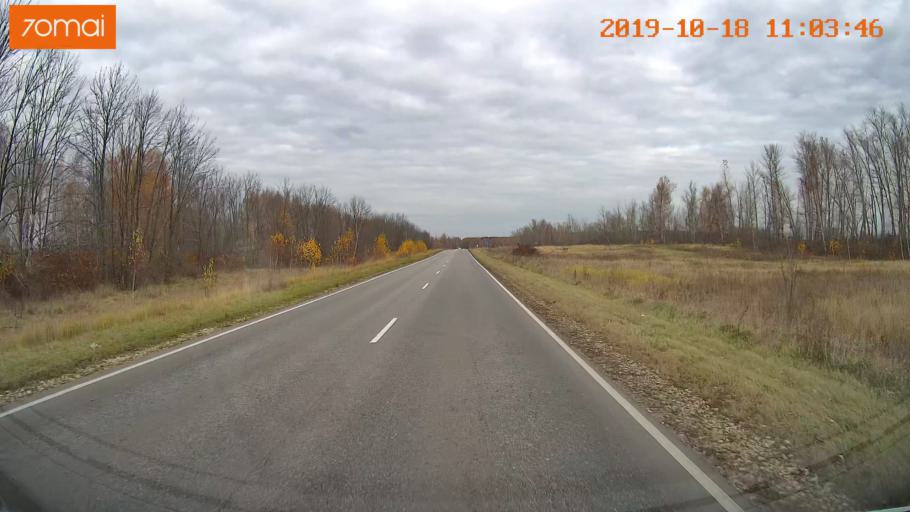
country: RU
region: Tula
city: Yepifan'
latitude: 53.8847
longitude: 38.5494
